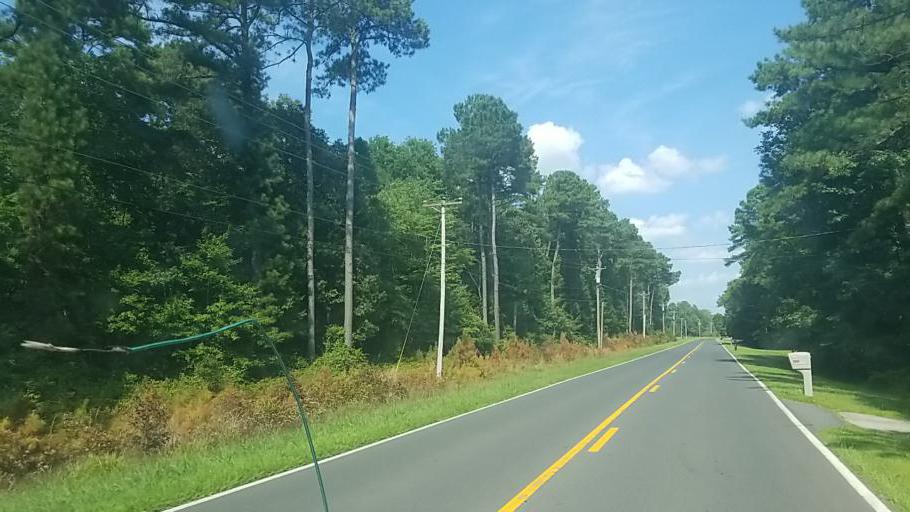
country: US
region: Maryland
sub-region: Wicomico County
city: Fruitland
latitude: 38.3134
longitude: -75.6401
